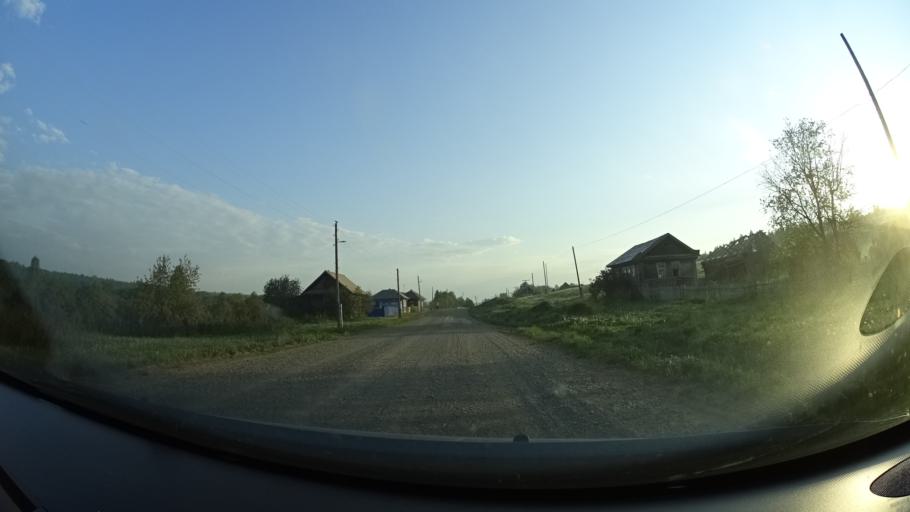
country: RU
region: Perm
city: Kuyeda
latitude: 56.6610
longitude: 55.6930
